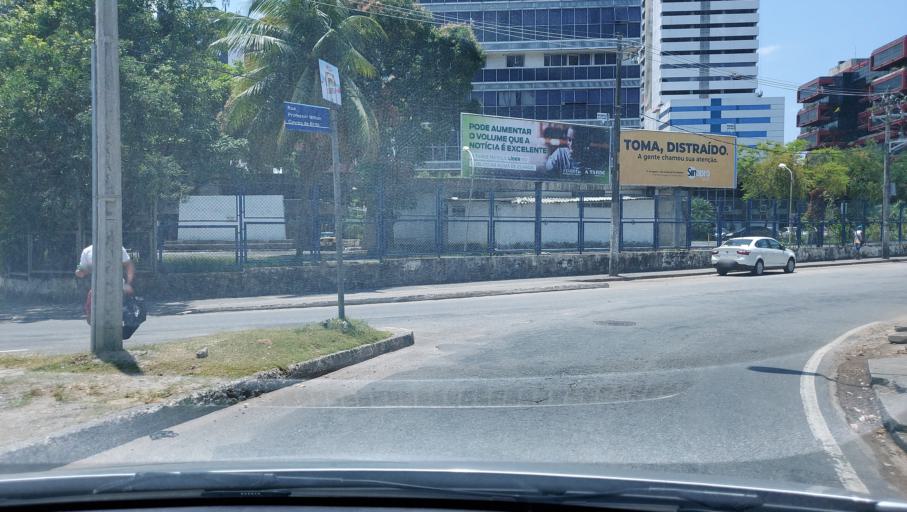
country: BR
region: Bahia
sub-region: Salvador
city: Salvador
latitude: -12.9806
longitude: -38.4583
